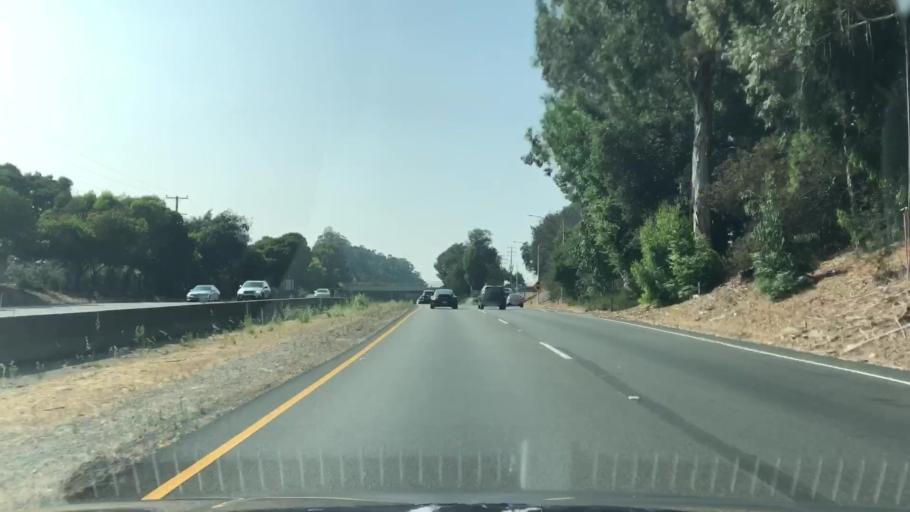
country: US
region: California
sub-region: Alameda County
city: Piedmont
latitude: 37.8091
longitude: -122.1953
